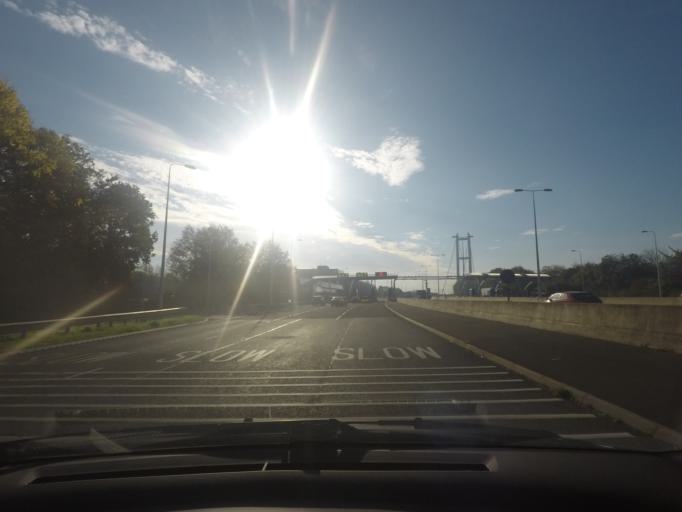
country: GB
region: England
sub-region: East Riding of Yorkshire
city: Hessle
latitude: 53.7209
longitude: -0.4522
